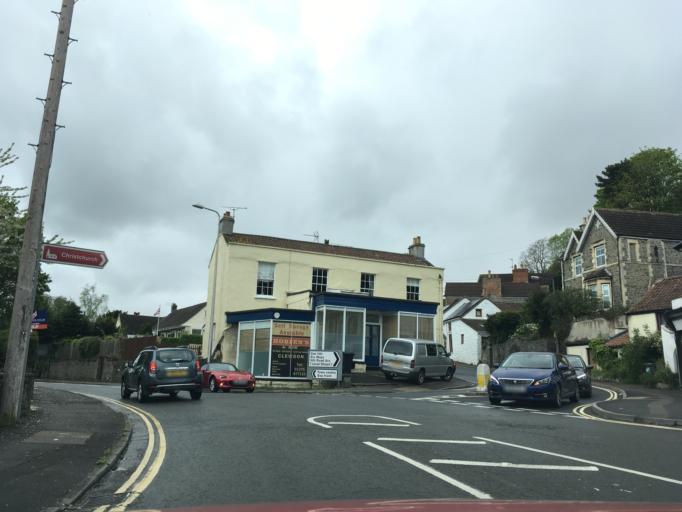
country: GB
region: England
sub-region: North Somerset
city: Clevedon
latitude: 51.4393
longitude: -2.8425
